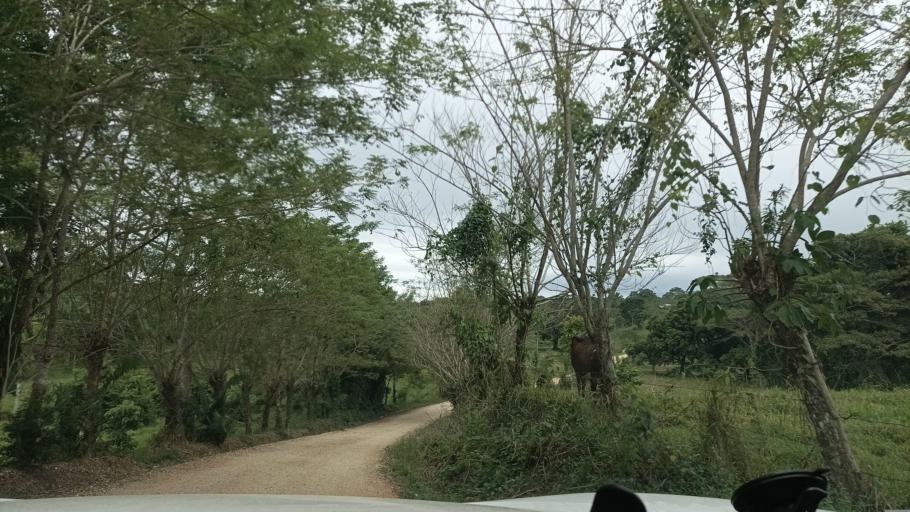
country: MX
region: Veracruz
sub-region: Uxpanapa
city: Poblado Cinco
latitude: 17.4812
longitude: -94.5721
